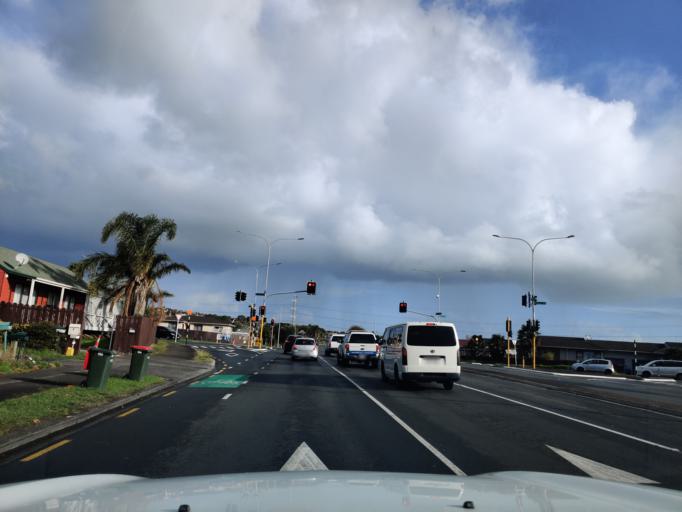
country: NZ
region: Auckland
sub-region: Auckland
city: Manukau City
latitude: -36.9776
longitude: 174.8980
